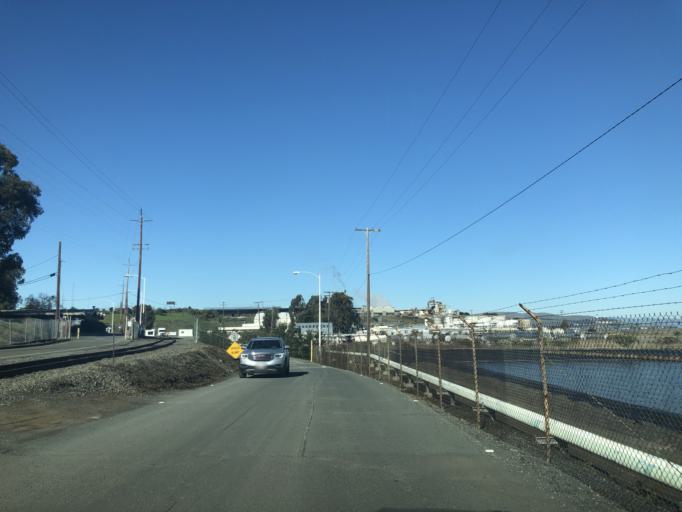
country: US
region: California
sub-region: Contra Costa County
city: Mountain View
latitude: 38.0278
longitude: -122.1126
